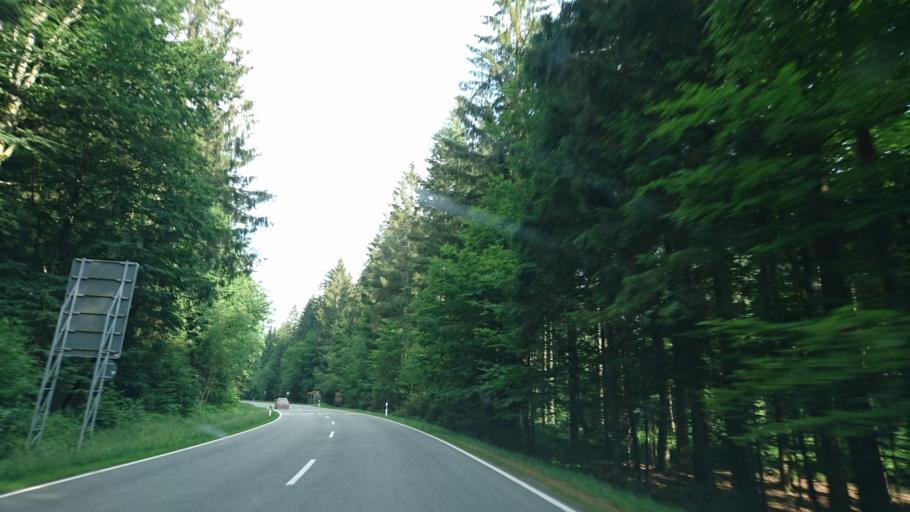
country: DE
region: Bavaria
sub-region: Lower Bavaria
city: Neuschonau
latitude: 48.9019
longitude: 13.4698
